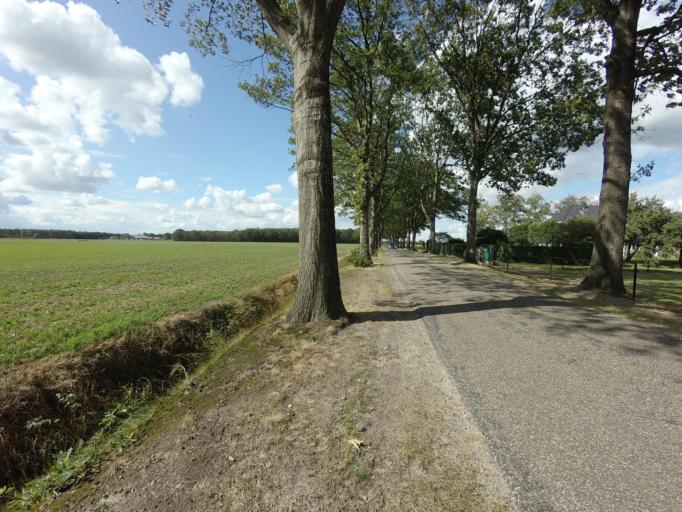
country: NL
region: Friesland
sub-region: Gemeente Weststellingwerf
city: Noordwolde
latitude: 52.9591
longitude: 6.2067
